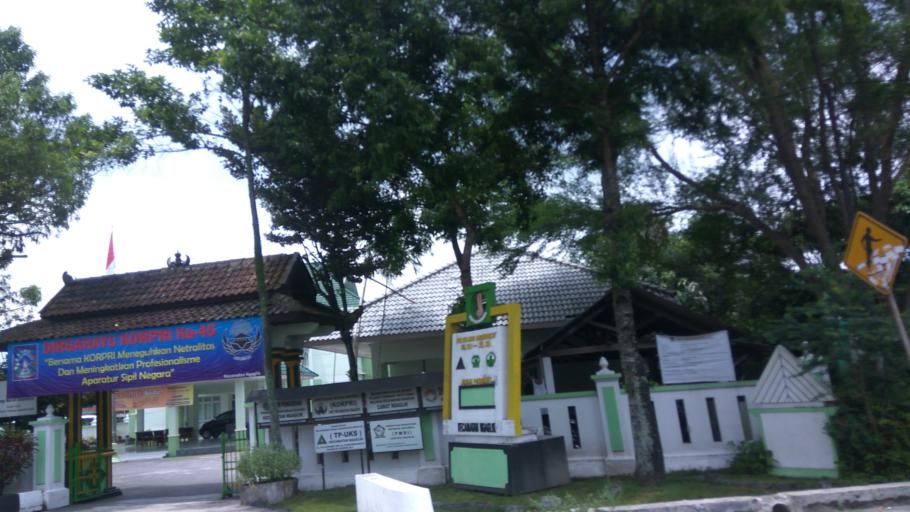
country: ID
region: Daerah Istimewa Yogyakarta
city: Melati
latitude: -7.7241
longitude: 110.4014
